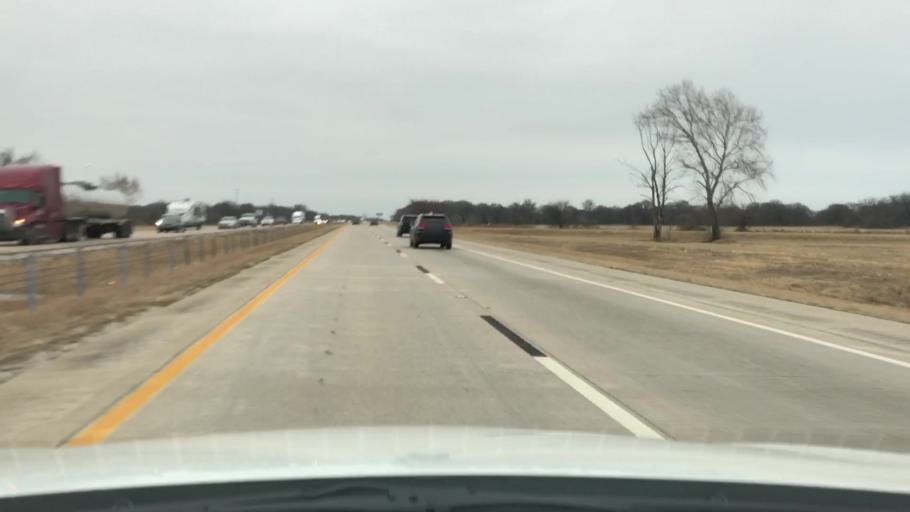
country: US
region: Oklahoma
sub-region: Love County
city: Marietta
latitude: 33.7959
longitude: -97.1348
